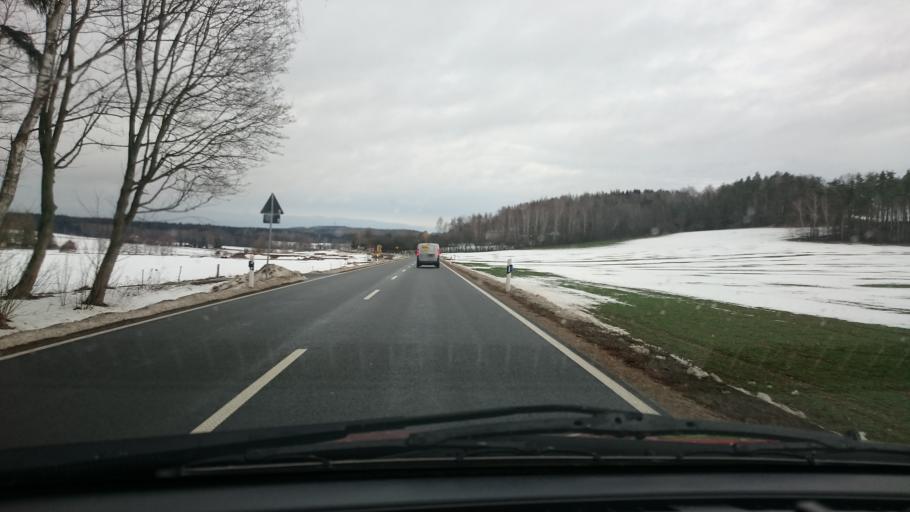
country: DE
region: Saxony
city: Waldkirchen
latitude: 50.6030
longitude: 12.4150
